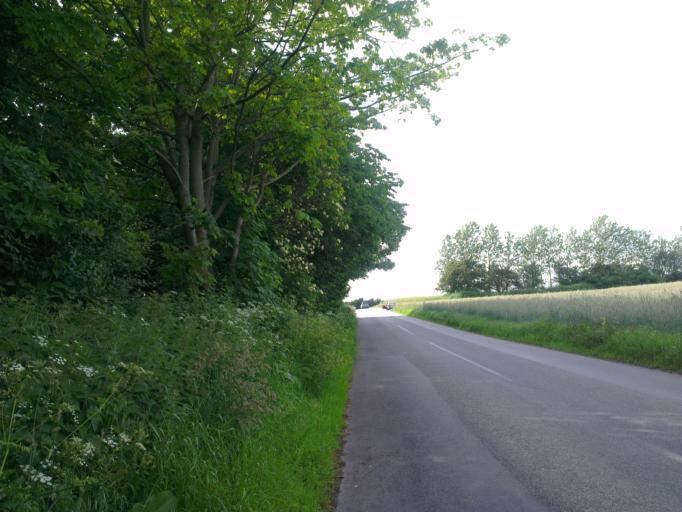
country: DK
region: Capital Region
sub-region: Frederikssund Kommune
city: Skibby
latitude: 55.7241
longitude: 11.9655
